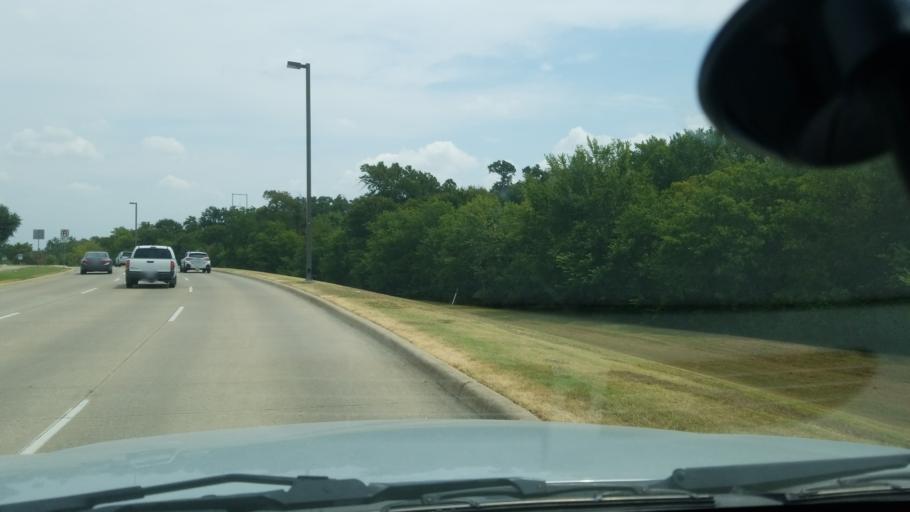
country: US
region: Texas
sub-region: Dallas County
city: Farmers Branch
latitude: 32.8757
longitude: -96.9315
